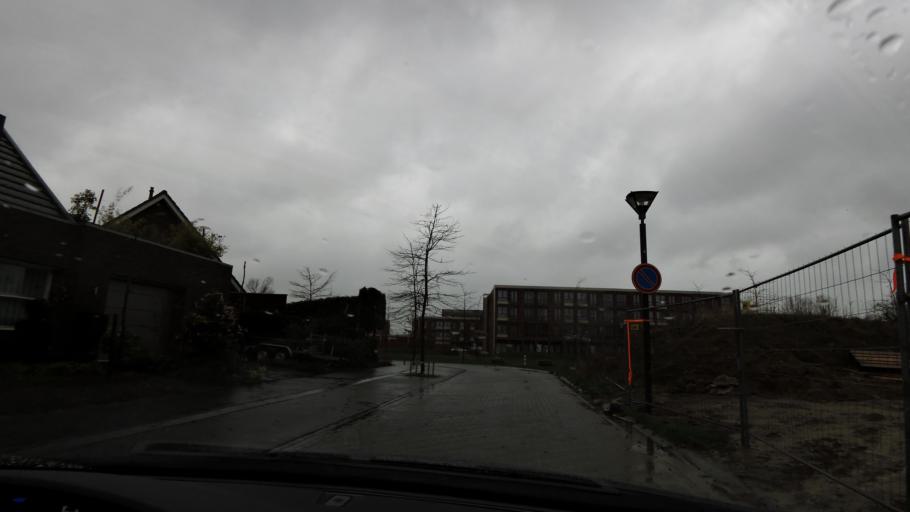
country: NL
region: Limburg
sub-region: Gemeente Sittard-Geleen
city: Born
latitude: 51.0372
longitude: 5.8193
